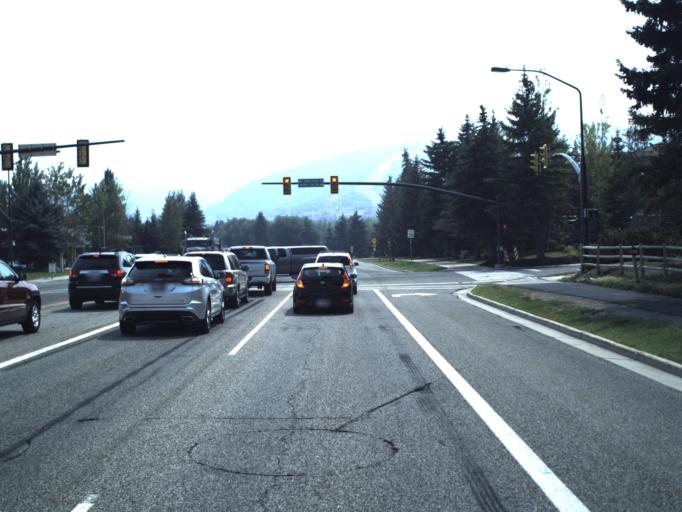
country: US
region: Utah
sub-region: Summit County
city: Park City
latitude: 40.6634
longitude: -111.5131
